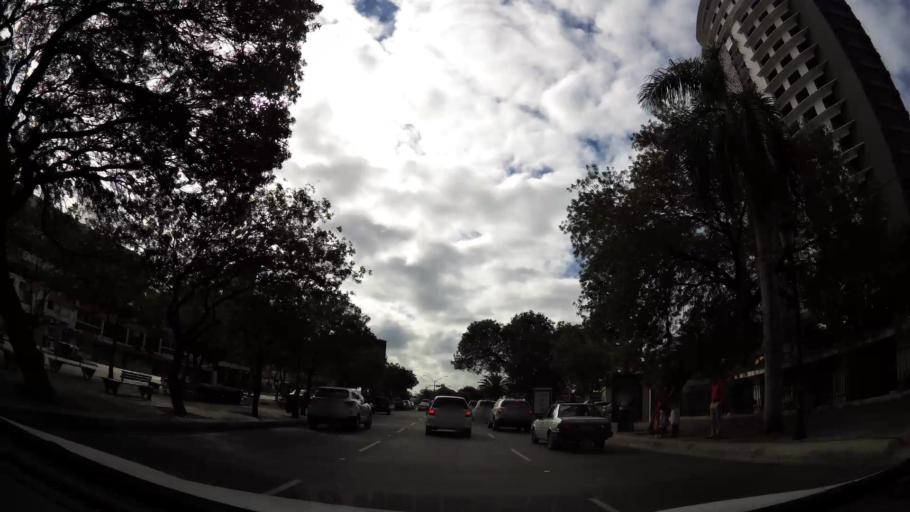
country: DO
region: Nacional
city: La Julia
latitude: 18.4593
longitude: -69.9331
